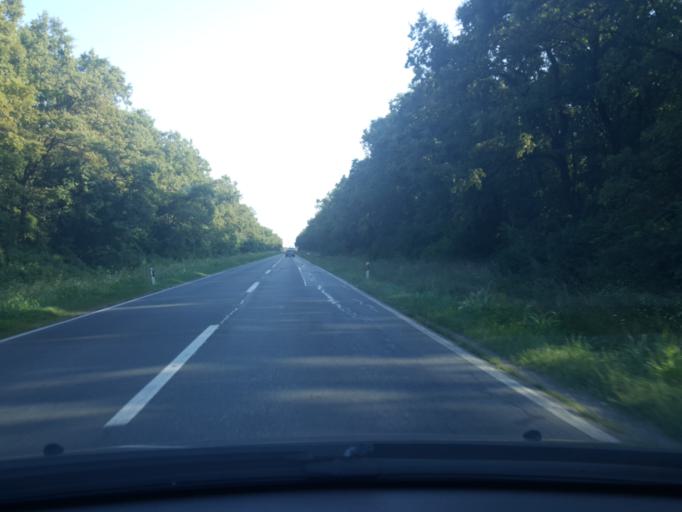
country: RS
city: Jarak
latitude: 44.9036
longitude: 19.7645
